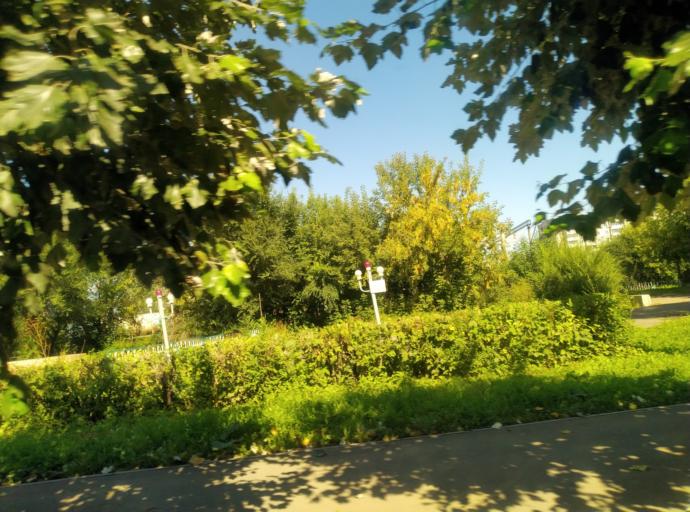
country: RU
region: Krasnoyarskiy
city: Krasnoyarsk
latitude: 55.9788
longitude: 92.8398
